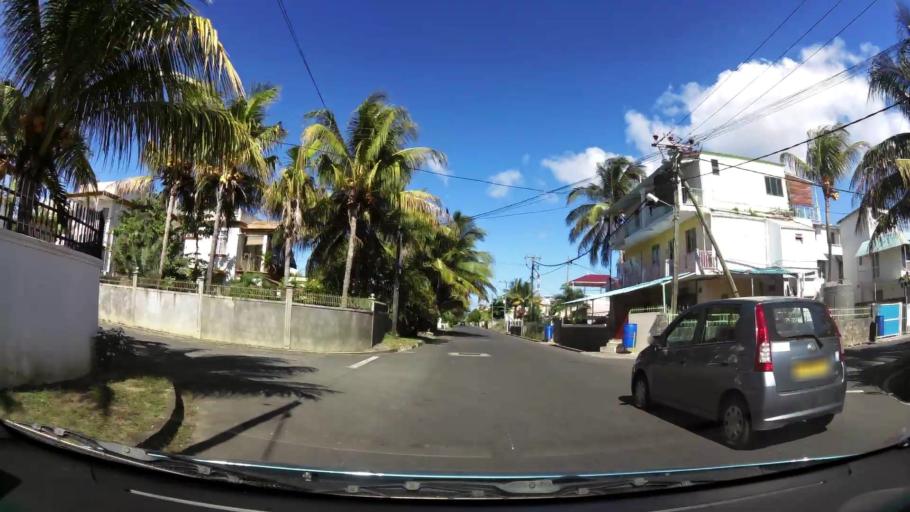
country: MU
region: Black River
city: Flic en Flac
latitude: -20.2871
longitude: 57.3671
